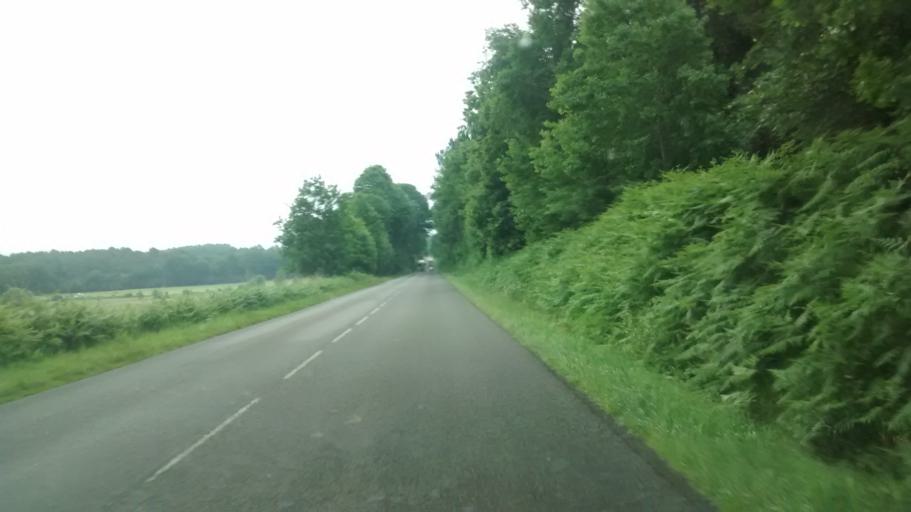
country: FR
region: Brittany
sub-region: Departement du Morbihan
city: Serent
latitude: 47.8171
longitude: -2.4609
